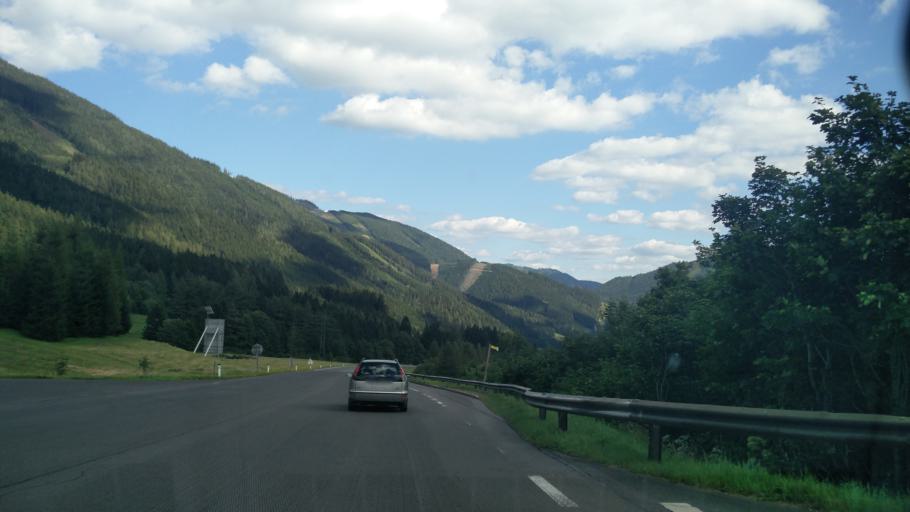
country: AT
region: Styria
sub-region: Politischer Bezirk Leoben
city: Vordernberg
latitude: 47.5141
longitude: 14.9707
